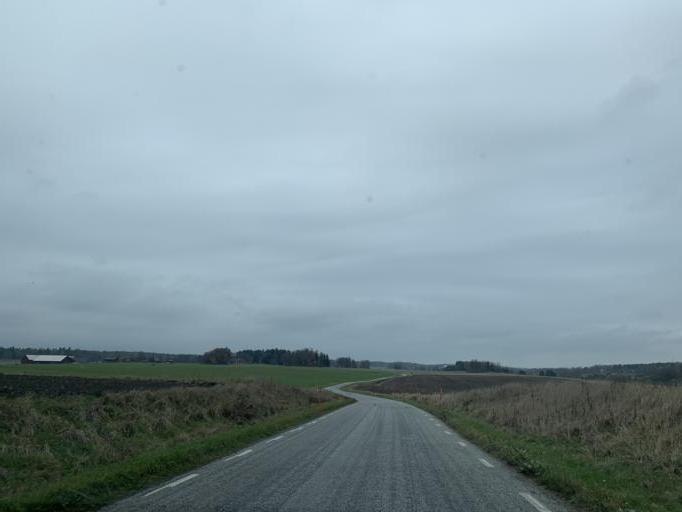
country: SE
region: Vaestmanland
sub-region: Vasteras
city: Skultuna
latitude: 59.6953
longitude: 16.4212
